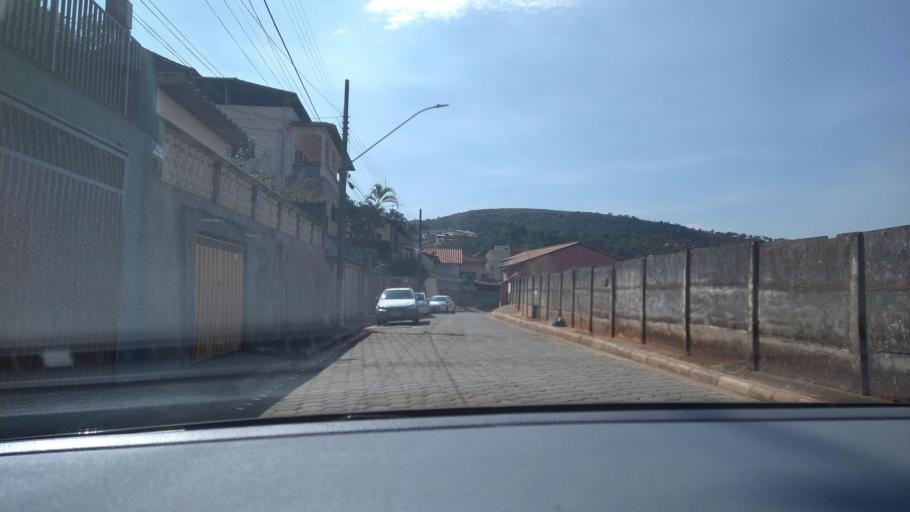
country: BR
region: Minas Gerais
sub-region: Rio Piracicaba
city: Rio Piracicaba
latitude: -19.9314
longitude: -43.1756
